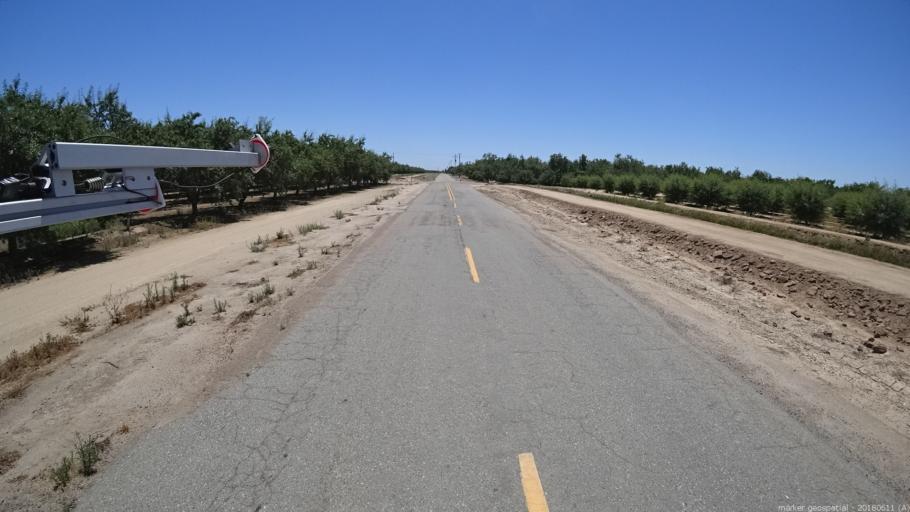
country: US
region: California
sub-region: Madera County
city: Fairmead
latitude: 37.0552
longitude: -120.1934
